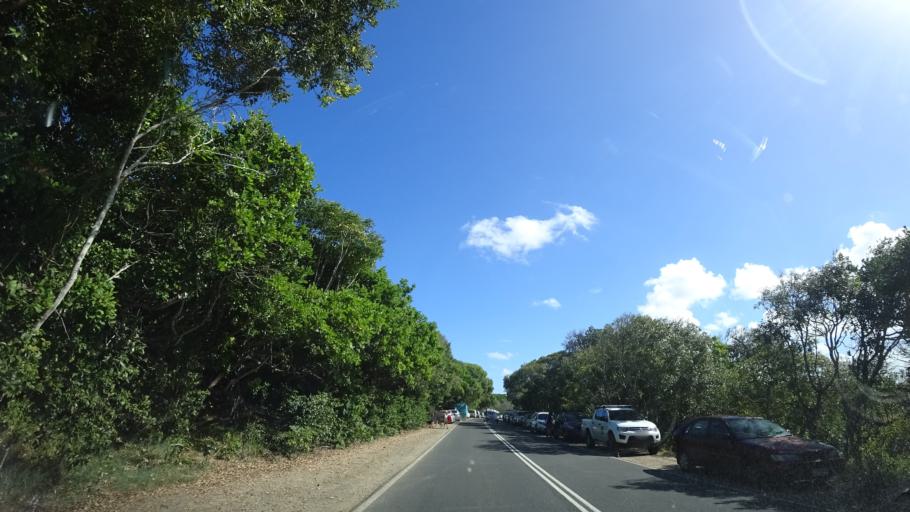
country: AU
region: Queensland
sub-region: Sunshine Coast
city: Mooloolaba
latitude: -26.6376
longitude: 153.1006
